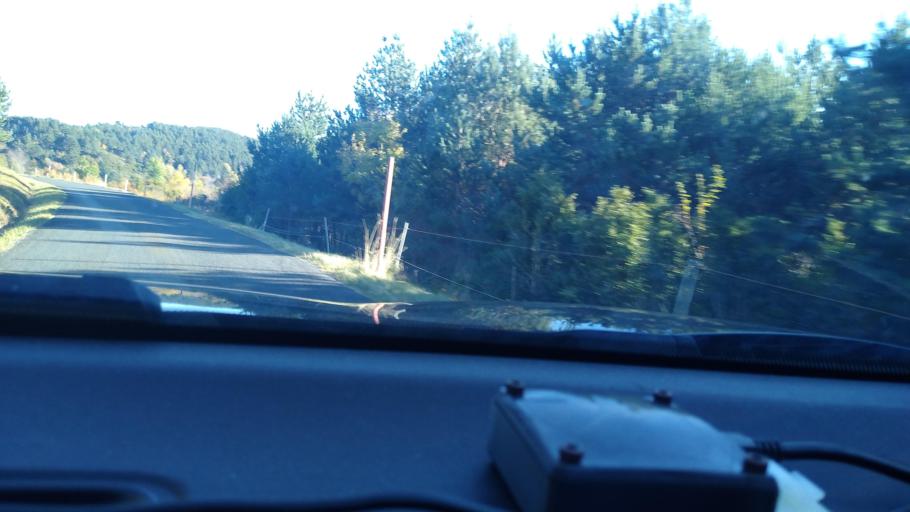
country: FR
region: Languedoc-Roussillon
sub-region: Departement de l'Aude
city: Quillan
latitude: 42.7388
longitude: 2.1439
